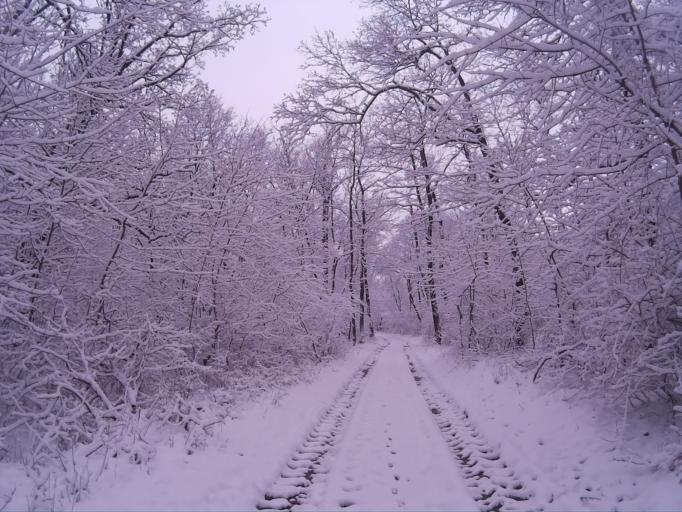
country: HU
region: Komarom-Esztergom
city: Tarjan
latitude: 47.5670
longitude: 18.5360
